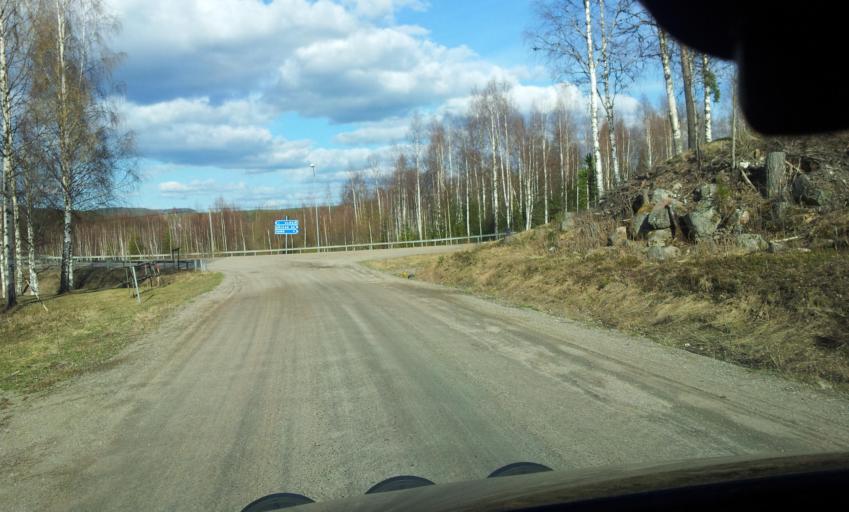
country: SE
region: Vaesternorrland
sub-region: Ange Kommun
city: Ange
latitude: 62.1797
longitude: 15.6302
